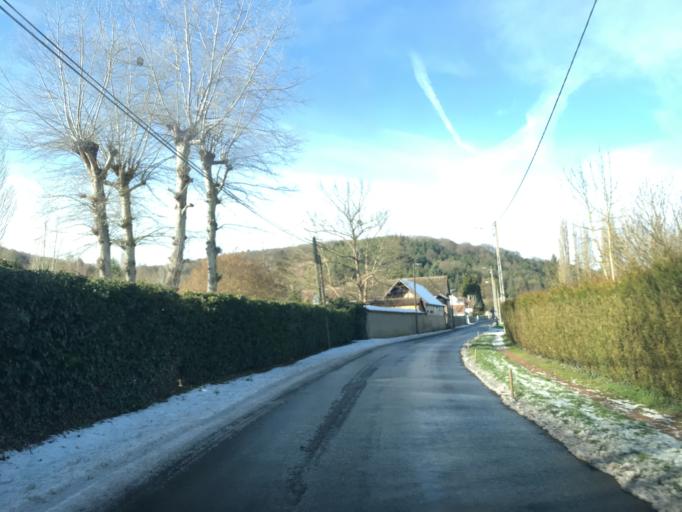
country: FR
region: Haute-Normandie
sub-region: Departement de l'Eure
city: Houlbec-Cocherel
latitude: 49.0710
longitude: 1.2854
